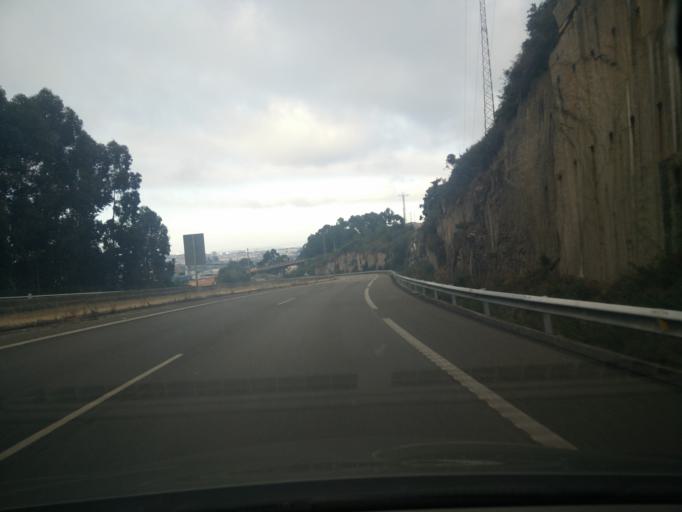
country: ES
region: Galicia
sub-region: Provincia da Coruna
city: Arteixo
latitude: 43.3387
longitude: -8.4538
